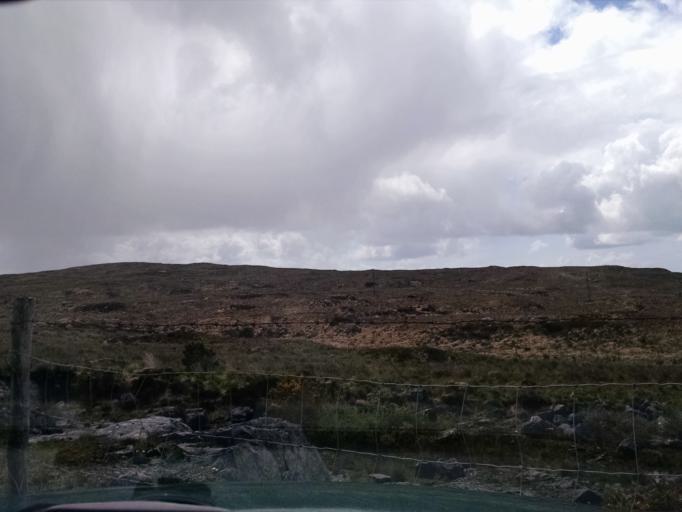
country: IE
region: Connaught
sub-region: County Galway
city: Oughterard
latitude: 53.3464
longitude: -9.5368
